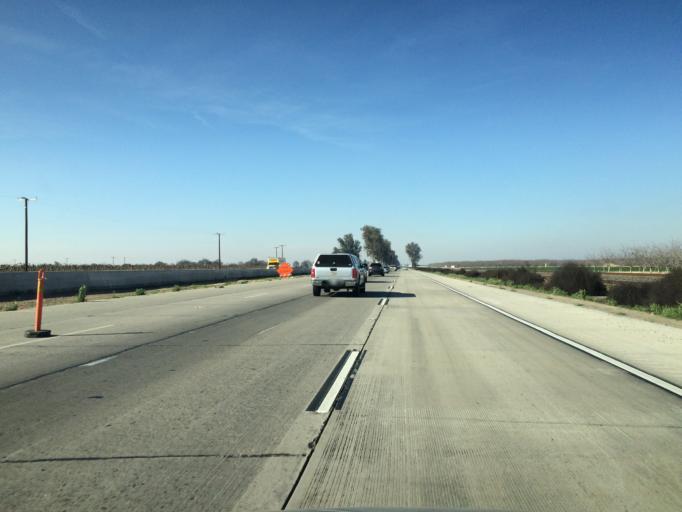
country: US
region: California
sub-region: Tulare County
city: Goshen
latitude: 36.3656
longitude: -119.4307
